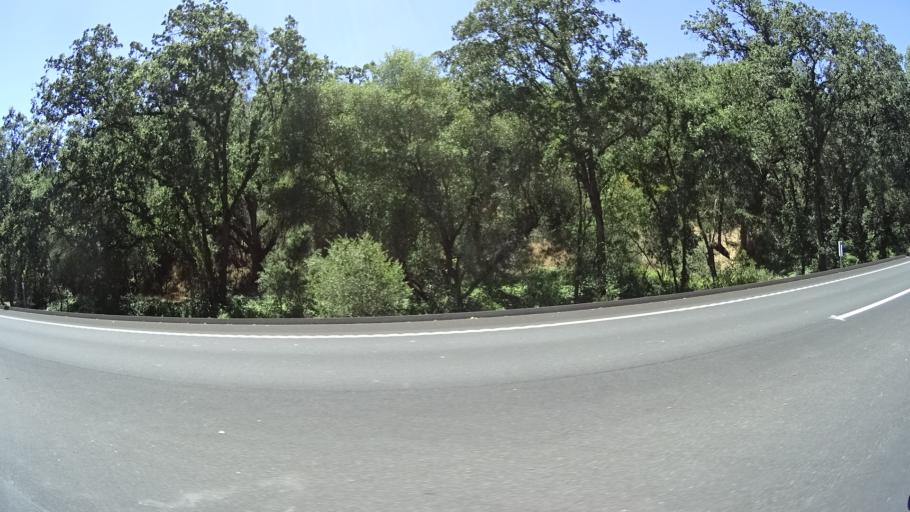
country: US
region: California
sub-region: Calaveras County
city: San Andreas
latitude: 38.2377
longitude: -120.7106
